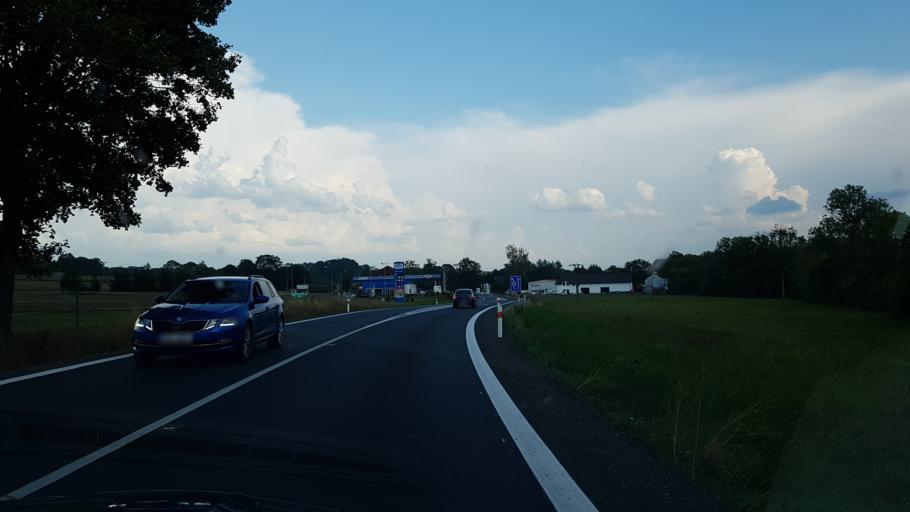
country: CZ
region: Pardubicky
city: Zamberk
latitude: 50.0944
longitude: 16.4236
